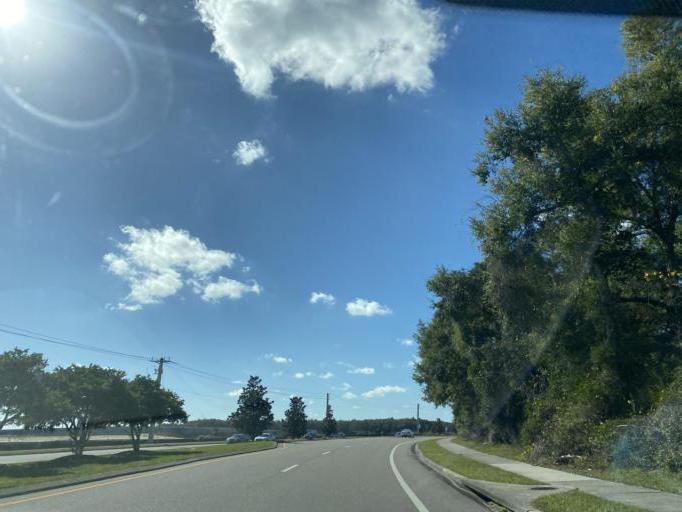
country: US
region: Florida
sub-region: Seminole County
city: Heathrow
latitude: 28.8004
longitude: -81.3486
